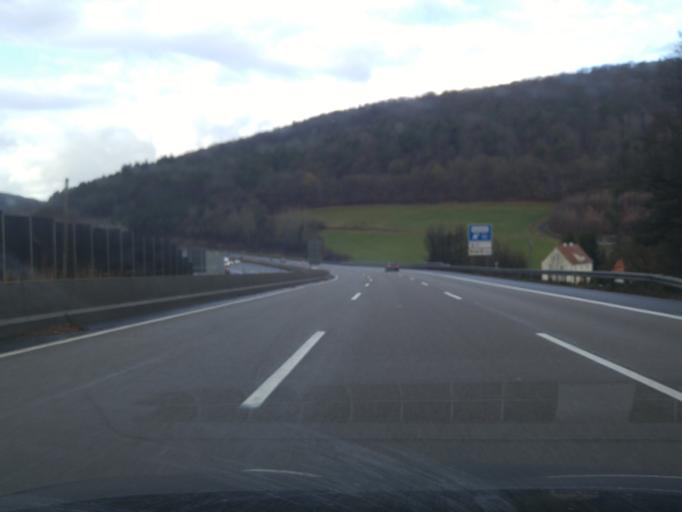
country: DE
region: Hesse
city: Schwarzenborn
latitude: 50.9684
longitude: 9.4791
